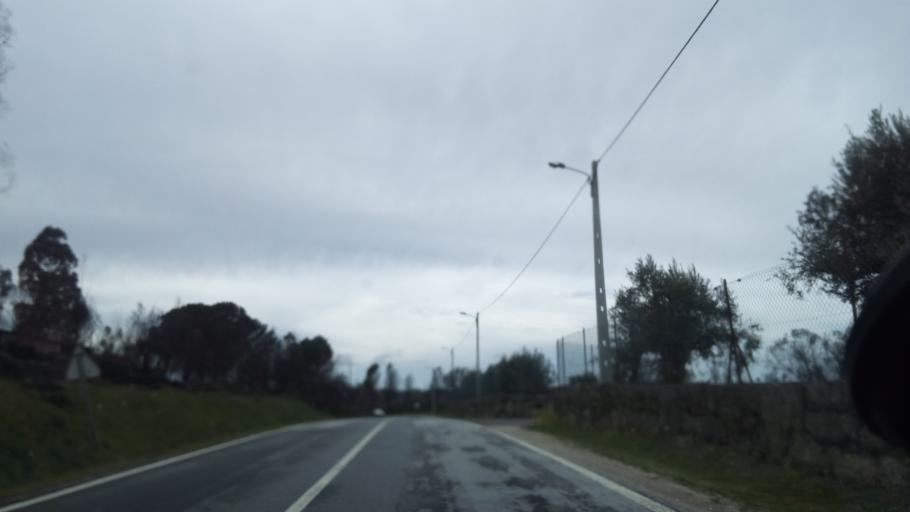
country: PT
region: Guarda
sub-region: Fornos de Algodres
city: Fornos de Algodres
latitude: 40.5214
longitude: -7.6163
